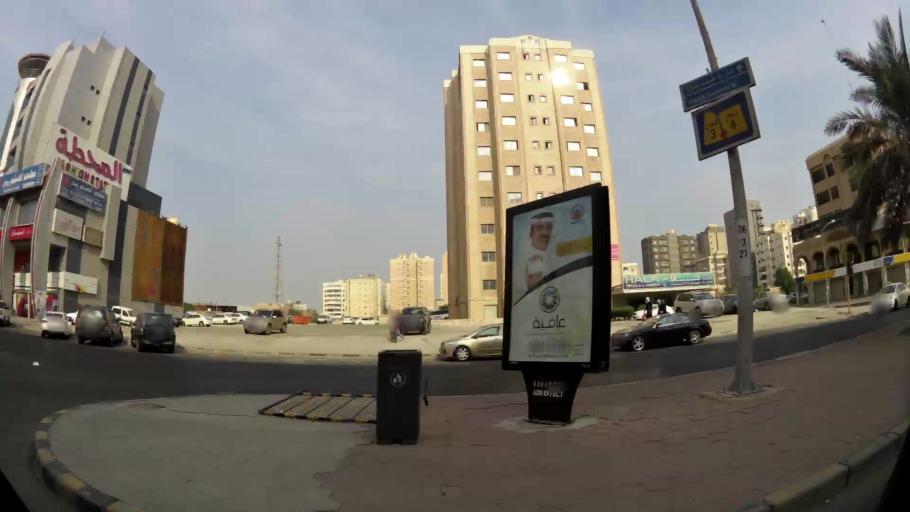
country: KW
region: Al Farwaniyah
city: Al Farwaniyah
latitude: 29.2758
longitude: 47.9638
